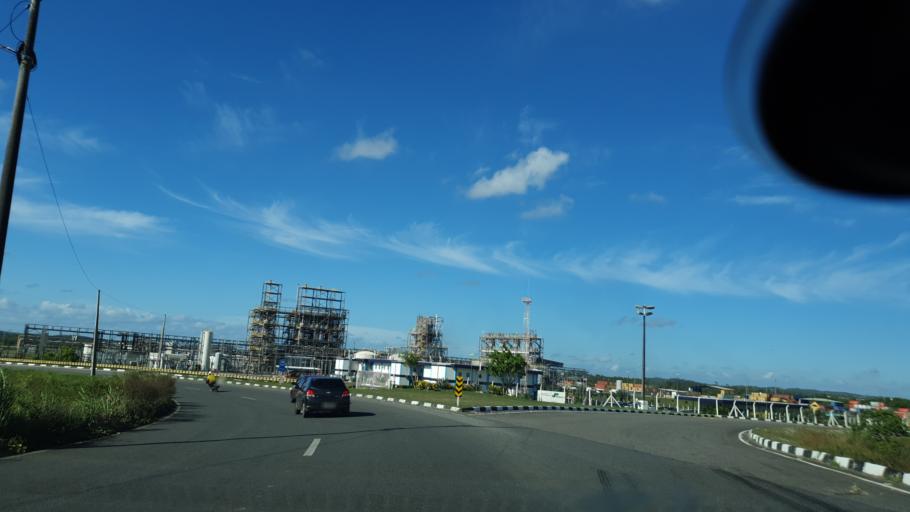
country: BR
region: Bahia
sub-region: Camacari
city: Camacari
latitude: -12.6595
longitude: -38.3013
